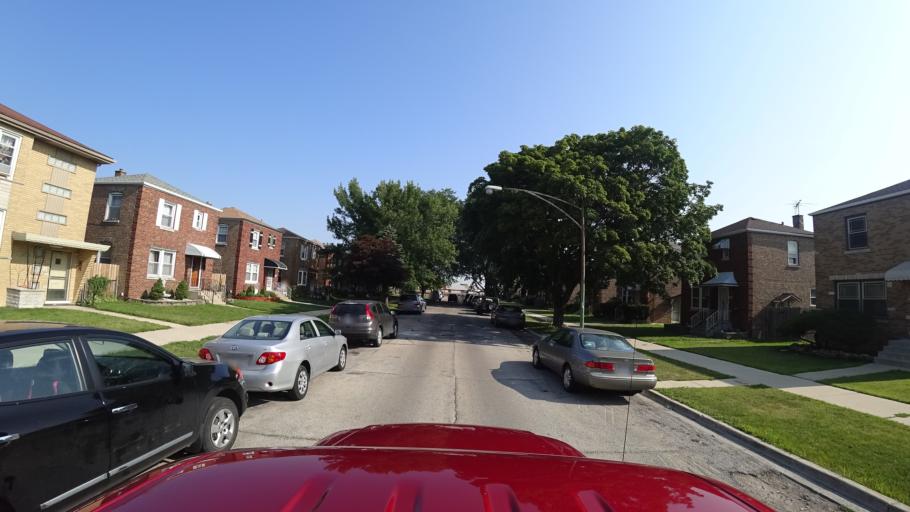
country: US
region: Illinois
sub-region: Cook County
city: Cicero
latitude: 41.8143
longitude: -87.7079
